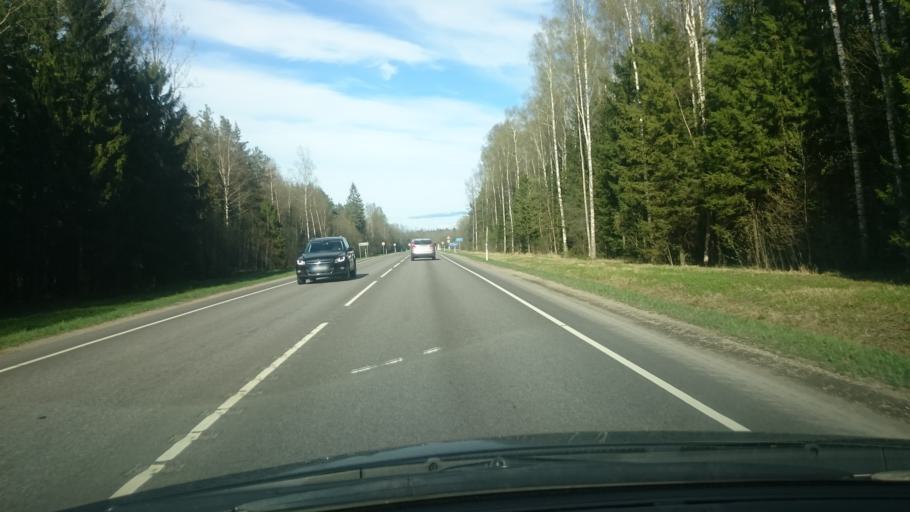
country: EE
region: Ida-Virumaa
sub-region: Toila vald
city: Voka
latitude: 59.3792
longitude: 27.5460
